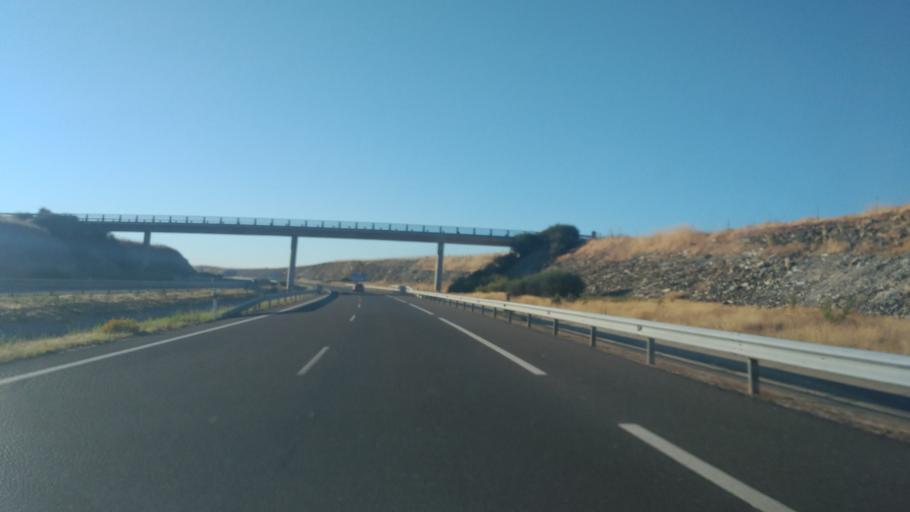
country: ES
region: Castille and Leon
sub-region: Provincia de Salamanca
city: Mozarbez
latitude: 40.8593
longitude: -5.6418
